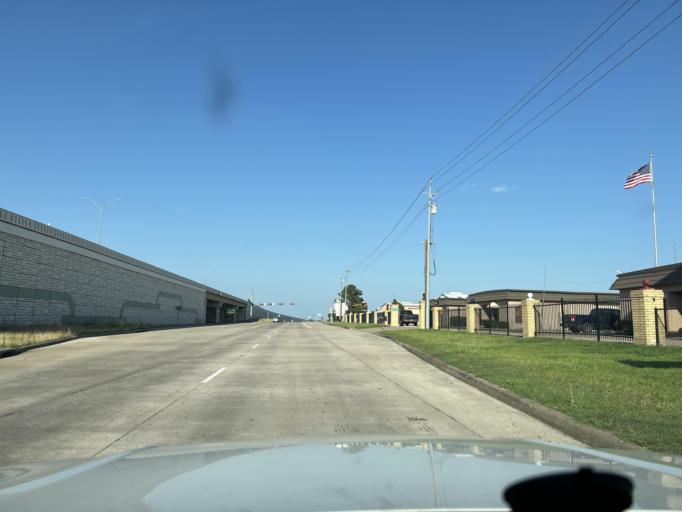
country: US
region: Texas
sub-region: Washington County
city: Brenham
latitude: 30.1428
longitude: -96.3705
